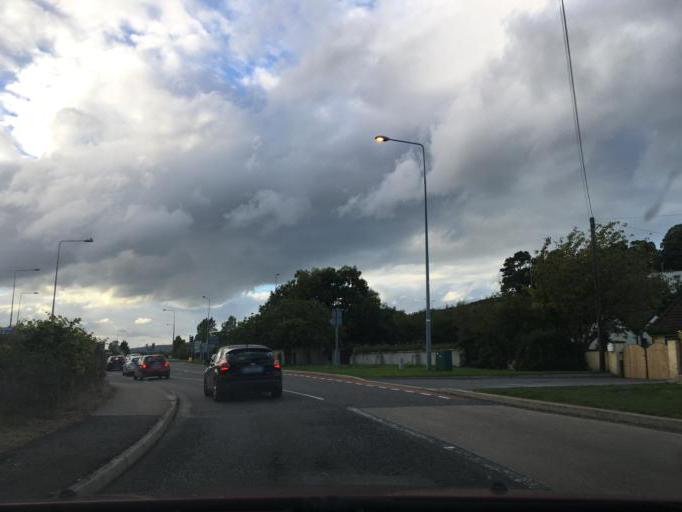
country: IE
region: Leinster
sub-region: Wicklow
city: Rathnew
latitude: 52.9885
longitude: -6.0660
